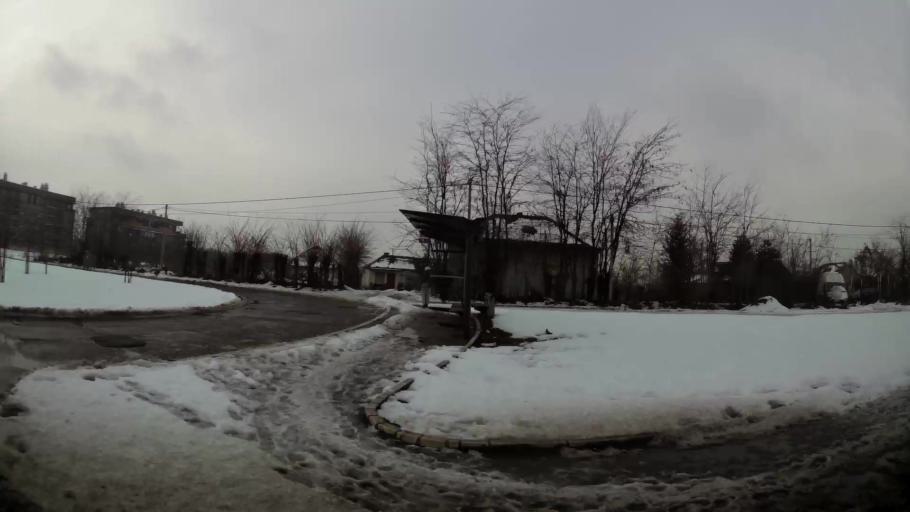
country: RS
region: Central Serbia
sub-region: Belgrade
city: Zemun
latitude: 44.8334
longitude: 20.3906
